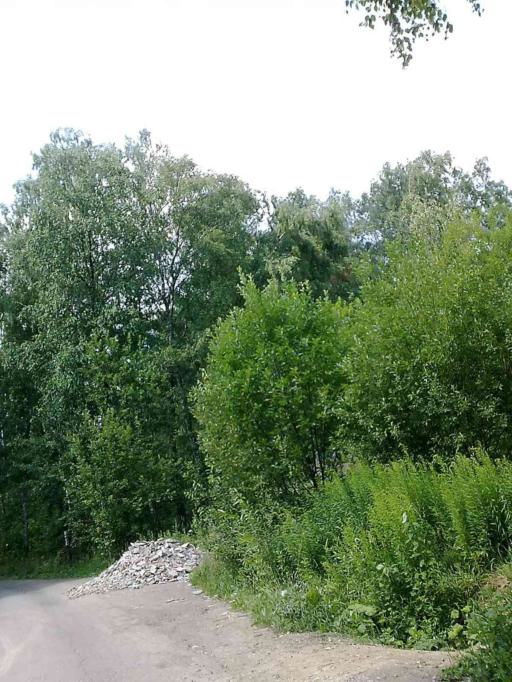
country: RU
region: Moskovskaya
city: Kommunarka
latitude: 55.5519
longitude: 37.4650
